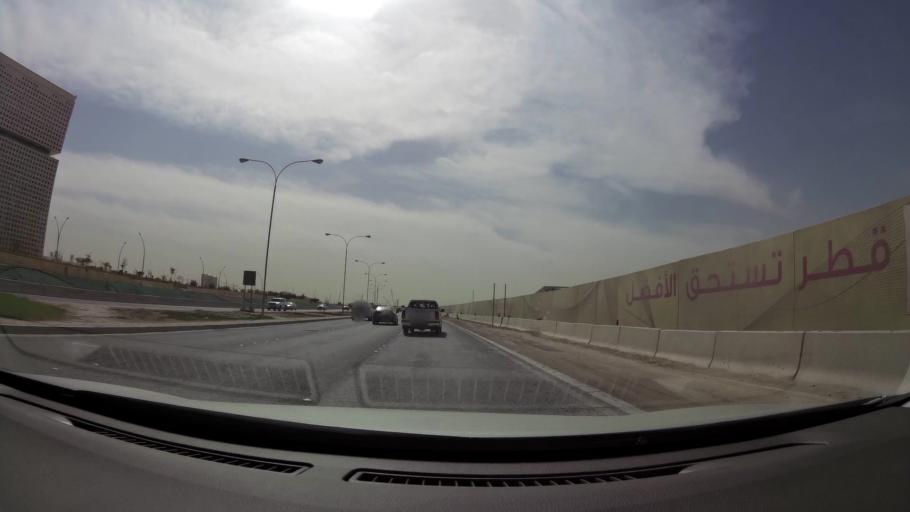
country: QA
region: Baladiyat ar Rayyan
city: Ar Rayyan
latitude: 25.3197
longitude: 51.4370
